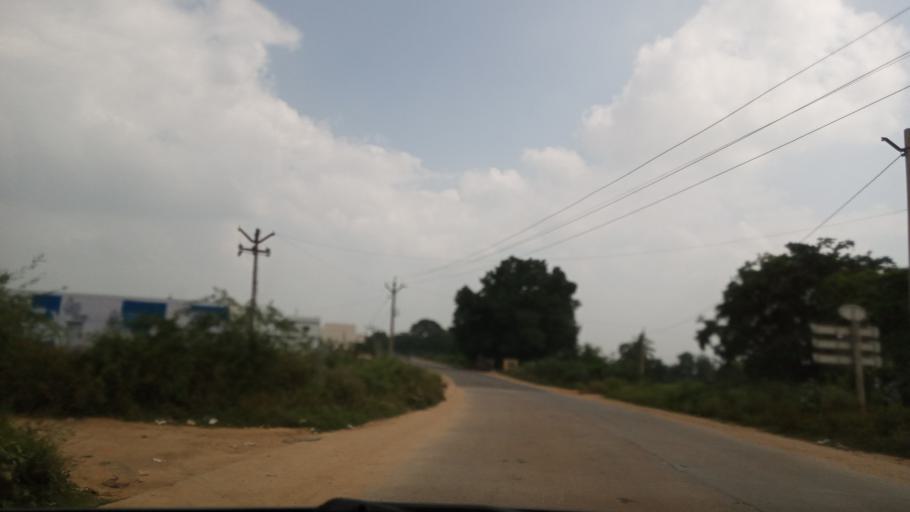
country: IN
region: Andhra Pradesh
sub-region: Chittoor
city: Madanapalle
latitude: 13.6374
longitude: 78.6369
